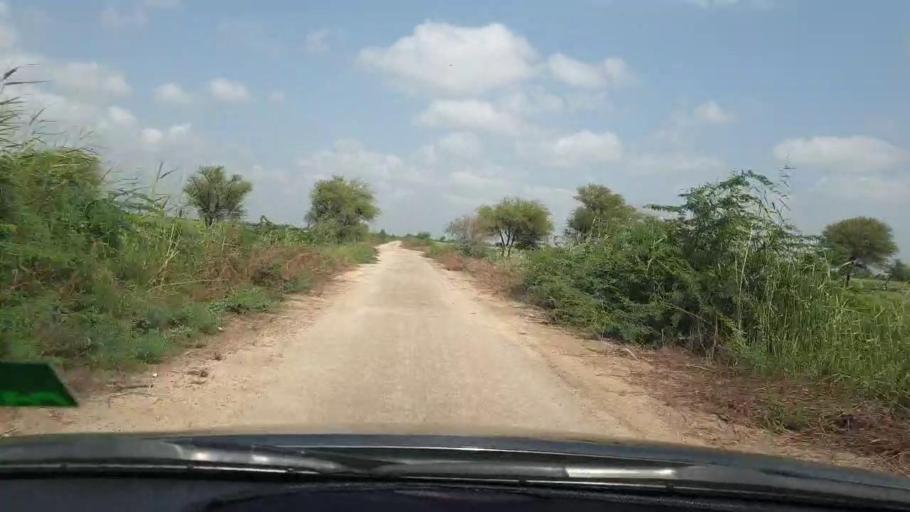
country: PK
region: Sindh
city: Tando Bago
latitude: 24.8656
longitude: 69.0355
